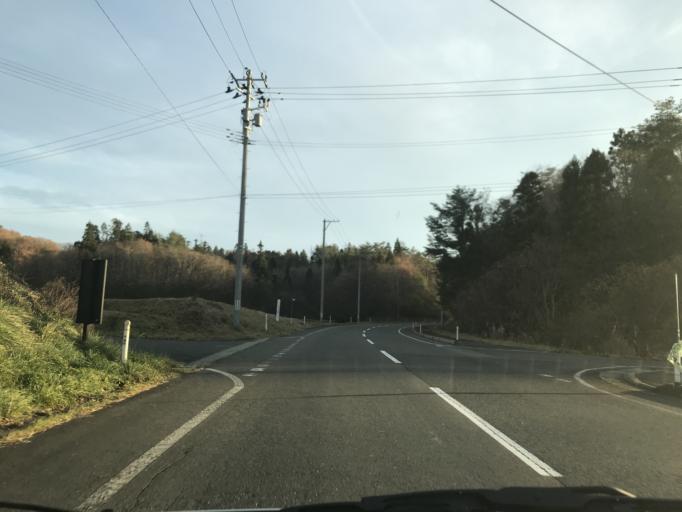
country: JP
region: Iwate
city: Ichinoseki
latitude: 38.9876
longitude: 141.0675
